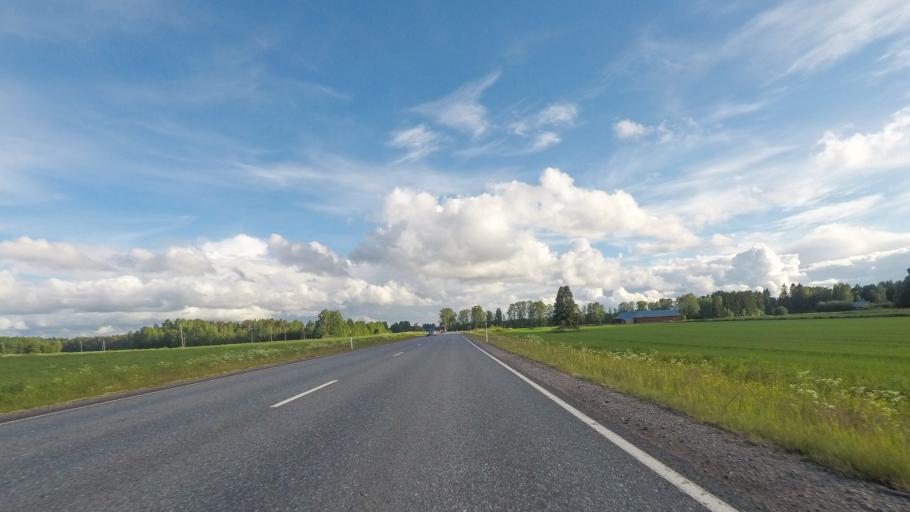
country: FI
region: Paijanne Tavastia
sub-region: Lahti
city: Hartola
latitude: 61.6167
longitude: 26.0081
